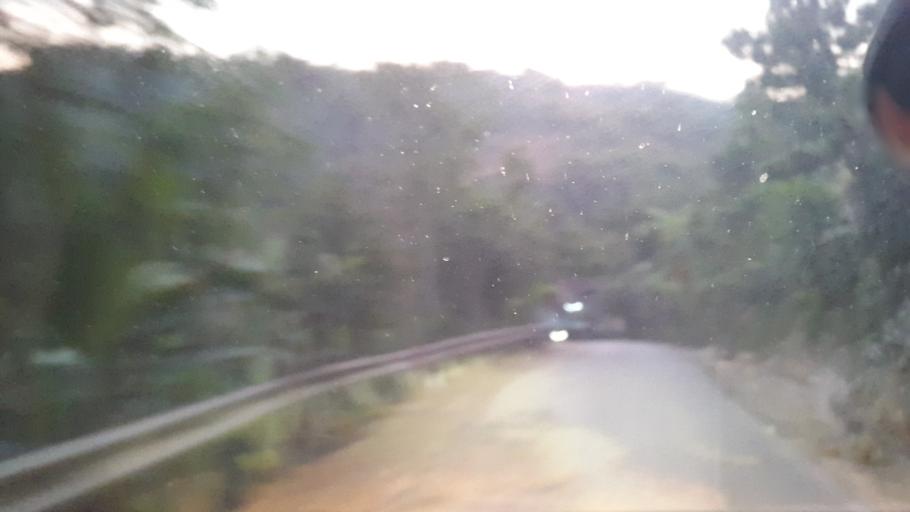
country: ID
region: West Java
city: Suryabakti
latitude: -6.9483
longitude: 106.8421
